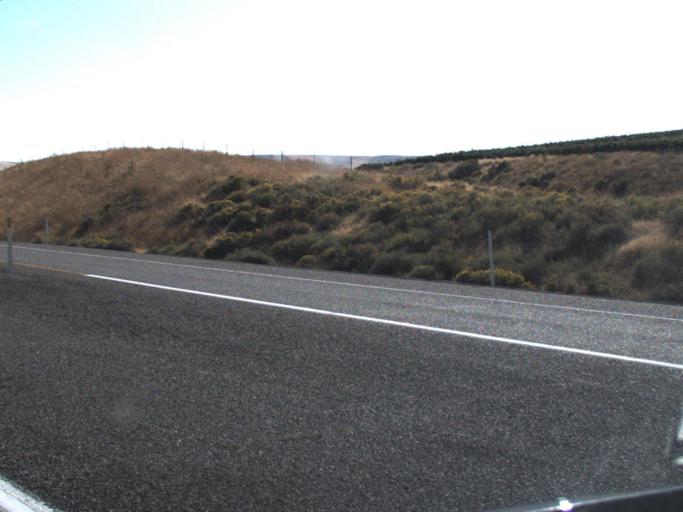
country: US
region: Washington
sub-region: Benton County
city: West Richland
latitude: 46.2203
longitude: -119.3500
